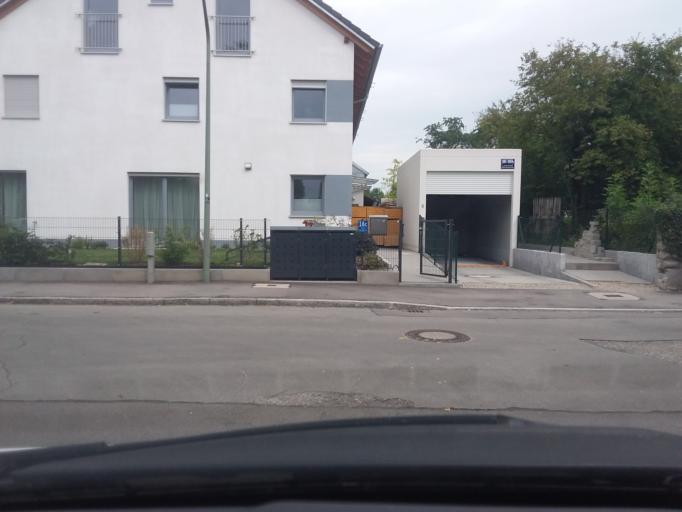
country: DE
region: Bavaria
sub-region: Upper Bavaria
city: Oberschleissheim
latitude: 48.2131
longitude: 11.5444
